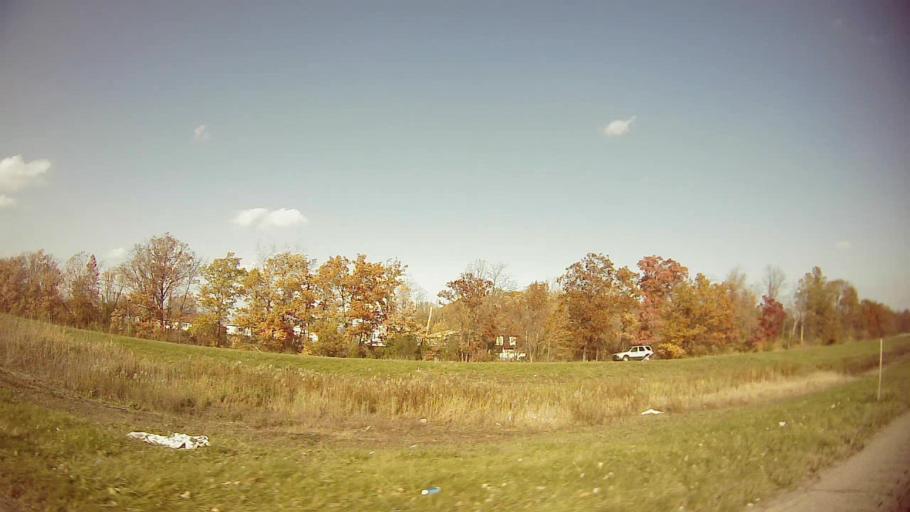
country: US
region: Michigan
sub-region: Wayne County
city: Taylor
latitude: 42.1901
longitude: -83.2612
